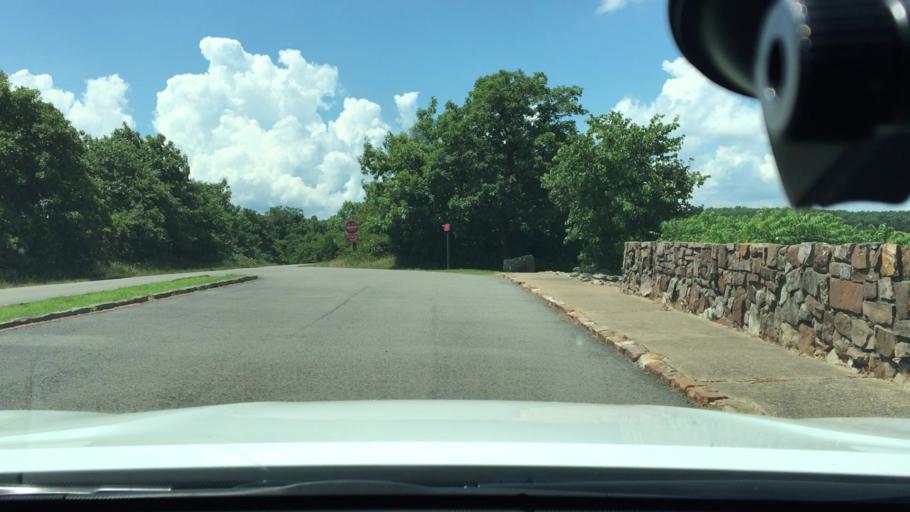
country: US
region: Arkansas
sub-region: Logan County
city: Paris
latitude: 35.1756
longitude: -93.6460
